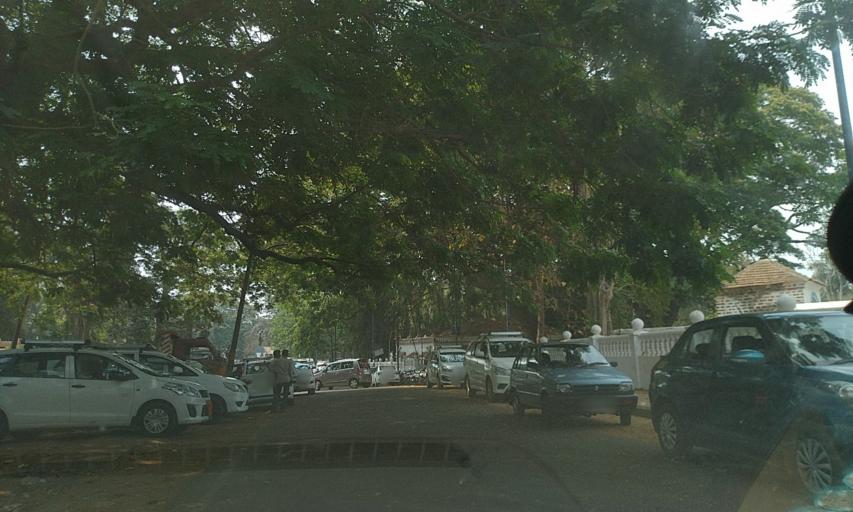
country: IN
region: Goa
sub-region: North Goa
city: Jua
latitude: 15.5023
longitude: 73.9135
